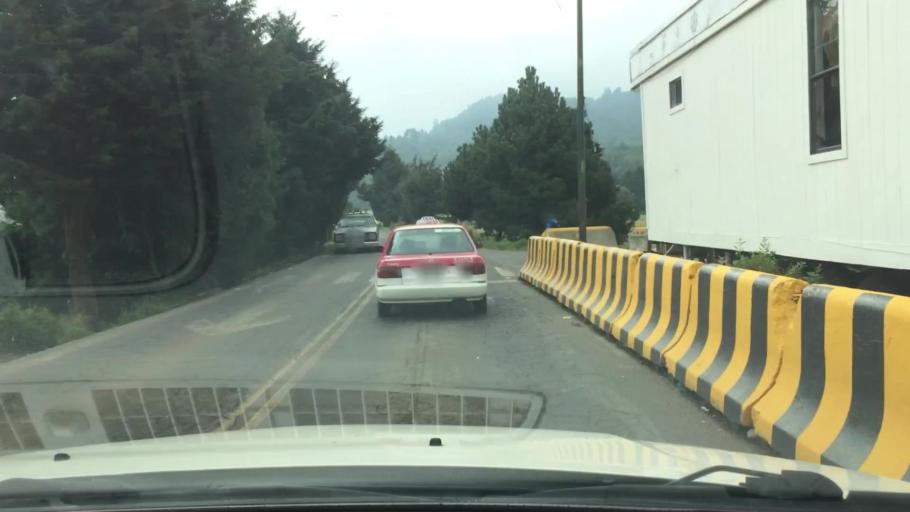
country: MX
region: Mexico City
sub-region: Tlalpan
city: Lomas de Tepemecatl
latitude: 19.2326
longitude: -99.2298
